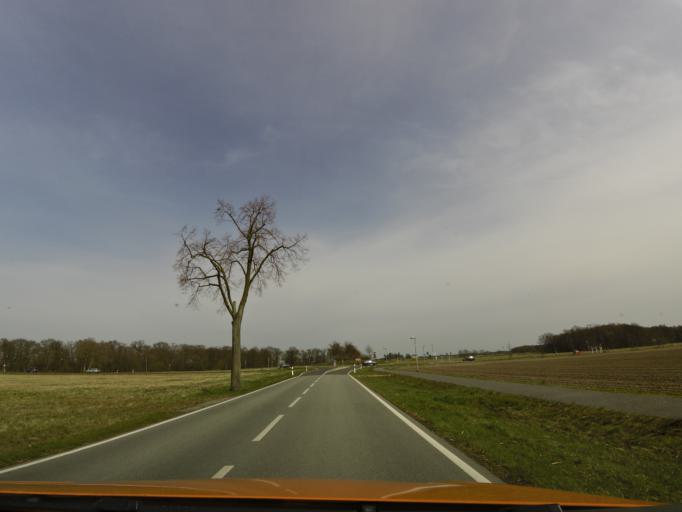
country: DE
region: Brandenburg
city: Stahnsdorf
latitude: 52.3301
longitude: 13.1716
